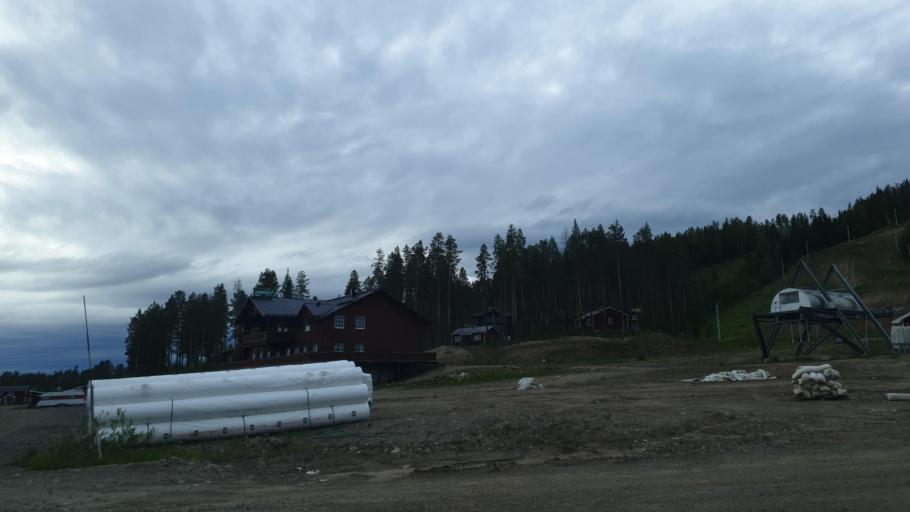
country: SE
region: Norrbotten
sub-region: Jokkmokks Kommun
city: Jokkmokk
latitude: 66.1545
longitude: 19.9902
